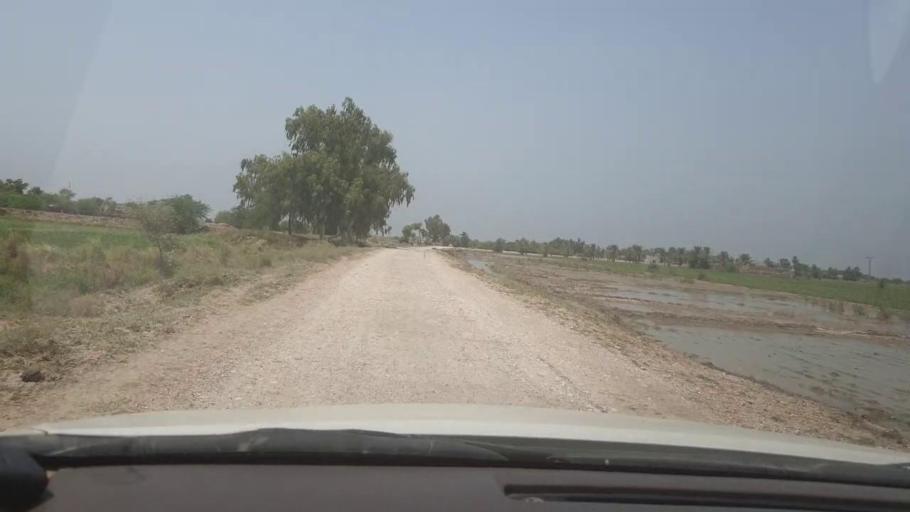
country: PK
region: Sindh
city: Shikarpur
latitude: 27.9432
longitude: 68.5722
